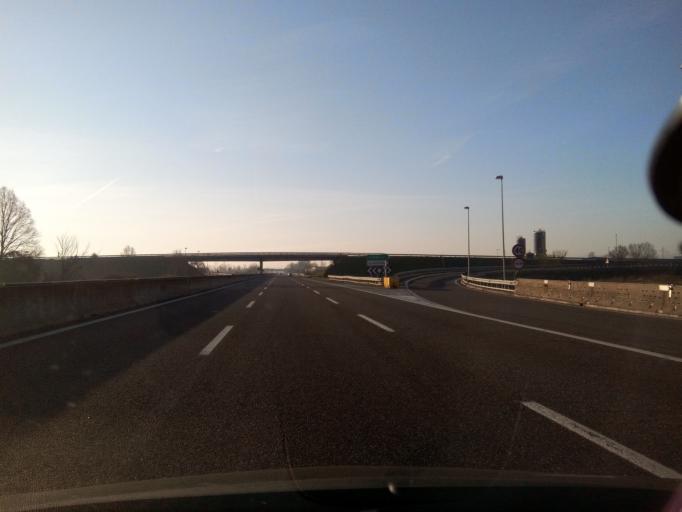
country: IT
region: Lombardy
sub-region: Provincia di Lodi
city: Guardamiglio
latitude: 45.1075
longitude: 9.6903
